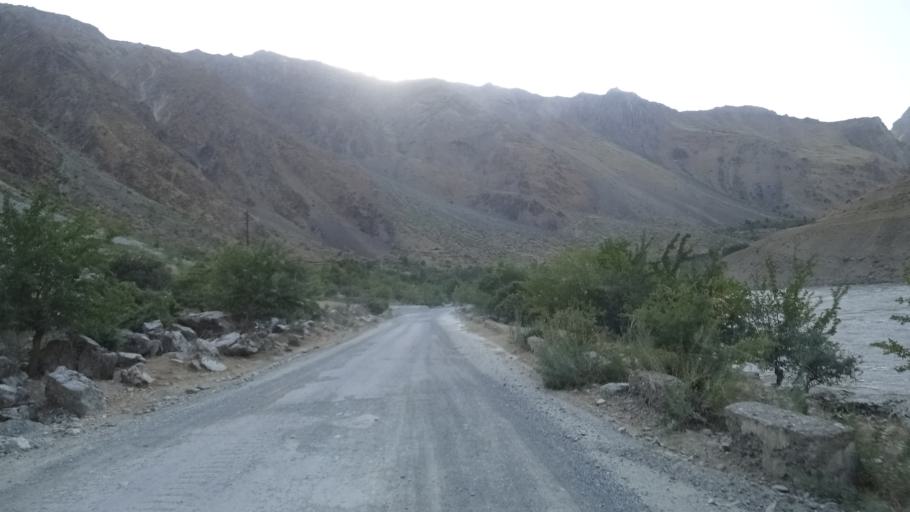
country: TJ
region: Gorno-Badakhshan
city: Qalaikhumb
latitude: 38.3865
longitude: 70.6787
